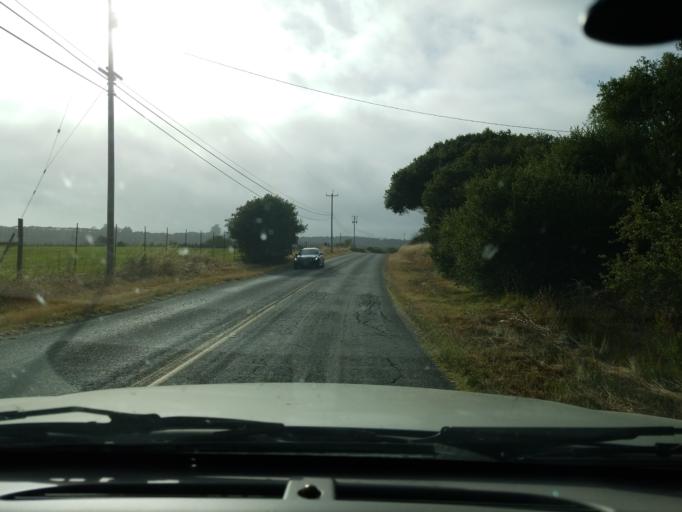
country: US
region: California
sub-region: Monterey County
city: Elkhorn
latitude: 36.8448
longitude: -121.7469
